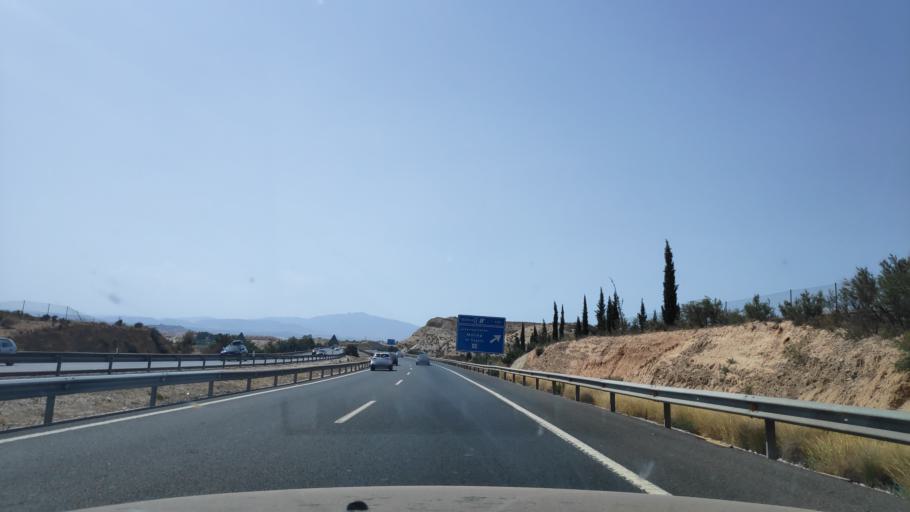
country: ES
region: Murcia
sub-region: Murcia
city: Molina de Segura
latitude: 38.0537
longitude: -1.1793
